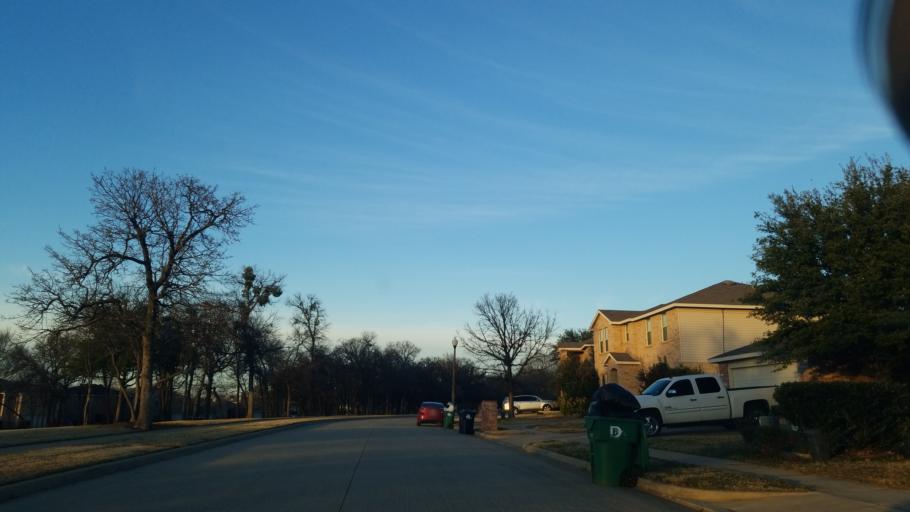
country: US
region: Texas
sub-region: Denton County
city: Corinth
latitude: 33.1542
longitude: -97.1015
